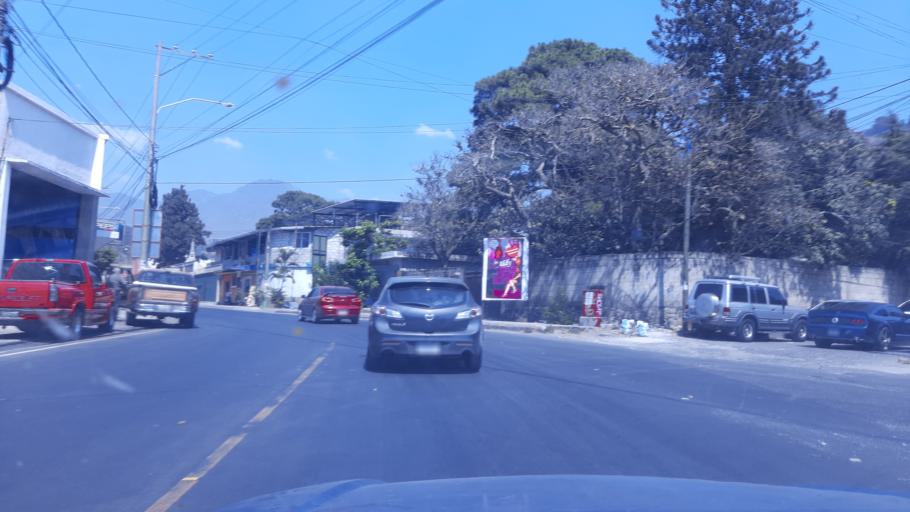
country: GT
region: Guatemala
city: Amatitlan
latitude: 14.4864
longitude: -90.6187
